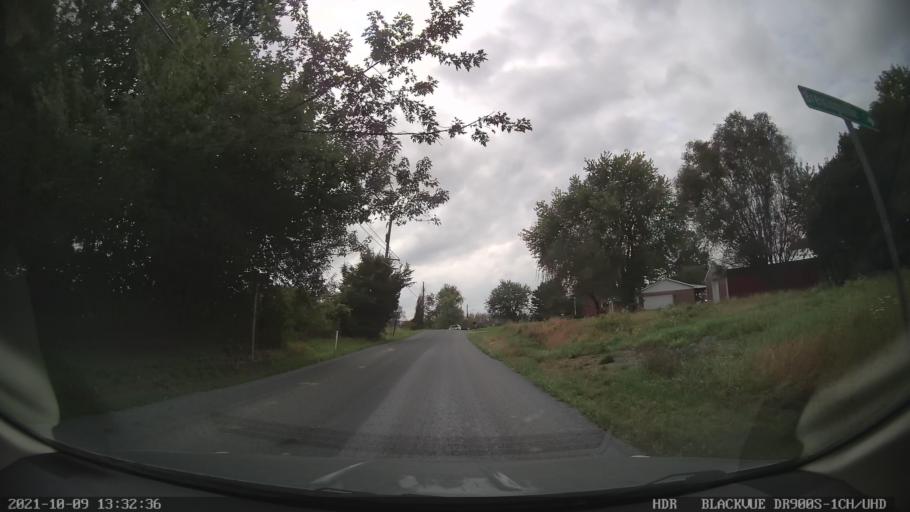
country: US
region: Pennsylvania
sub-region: Lehigh County
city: Breinigsville
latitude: 40.5240
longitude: -75.6238
